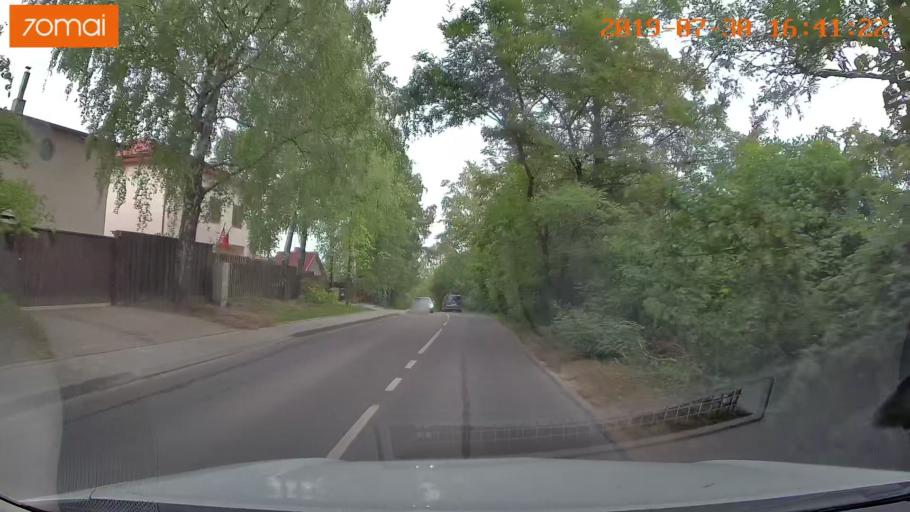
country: LT
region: Vilnius County
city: Rasos
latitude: 54.7108
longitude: 25.3563
